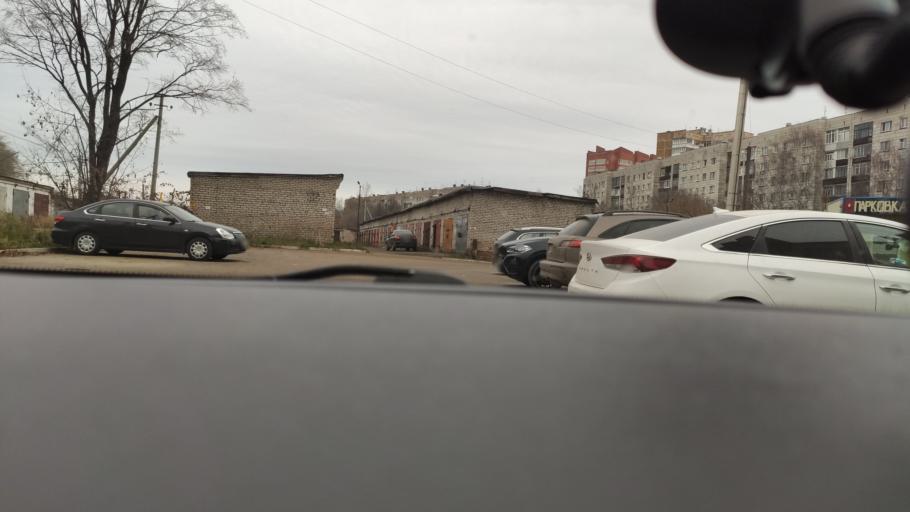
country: RU
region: Perm
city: Perm
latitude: 57.9866
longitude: 56.2304
